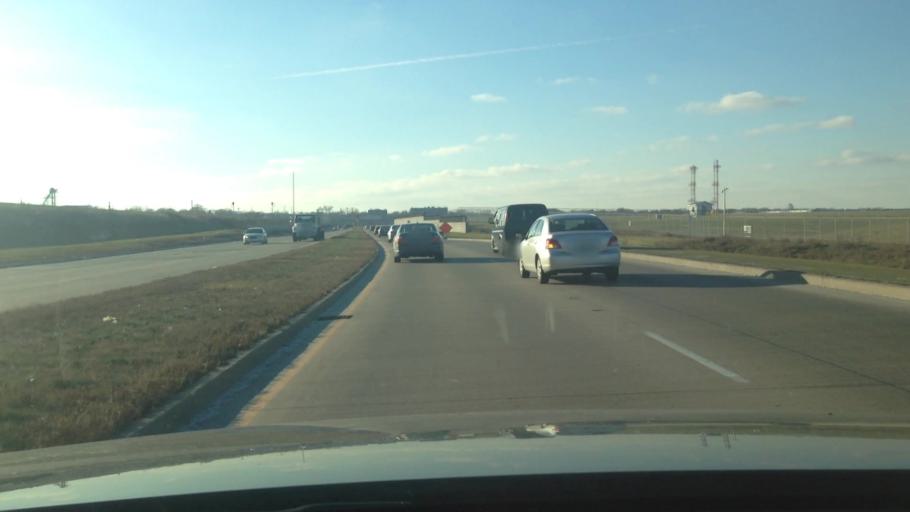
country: US
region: Illinois
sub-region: DuPage County
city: Bensenville
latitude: 41.9553
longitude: -87.9207
